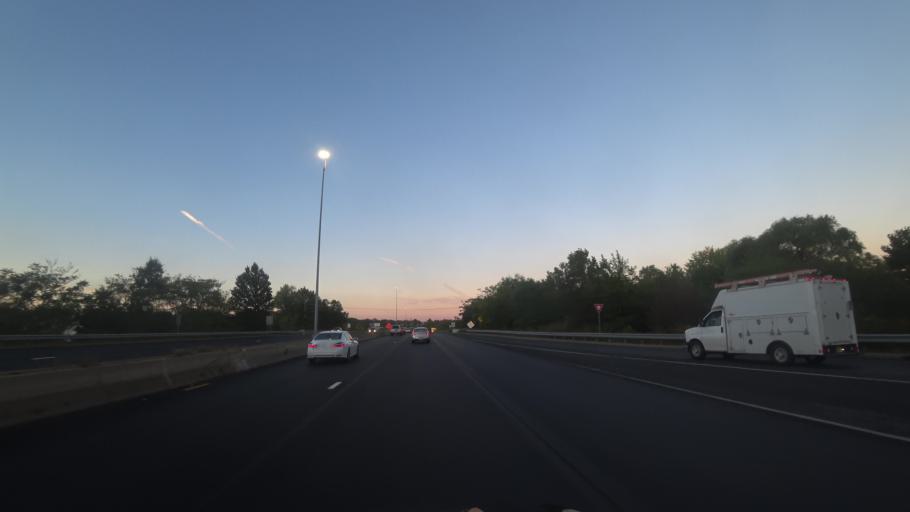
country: US
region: Massachusetts
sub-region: Suffolk County
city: Revere
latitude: 42.4278
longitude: -71.0202
